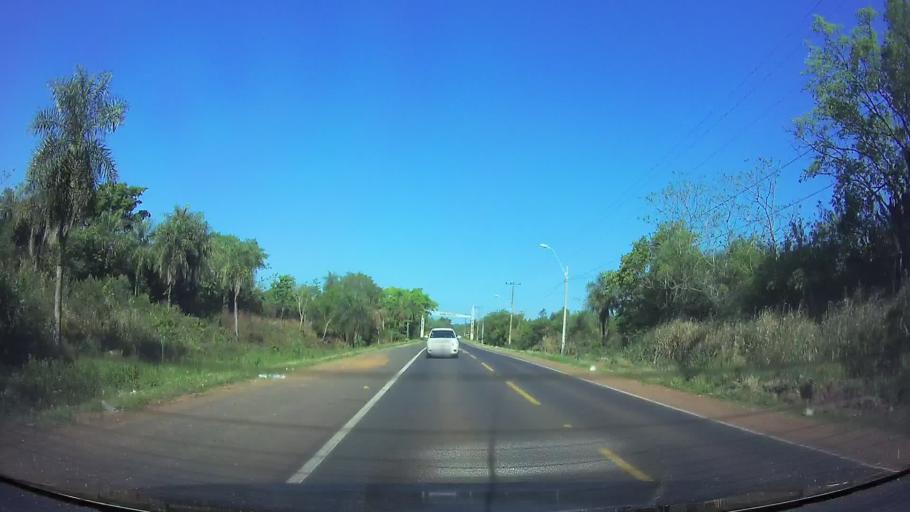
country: PY
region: Central
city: Itaugua
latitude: -25.3589
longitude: -57.3245
